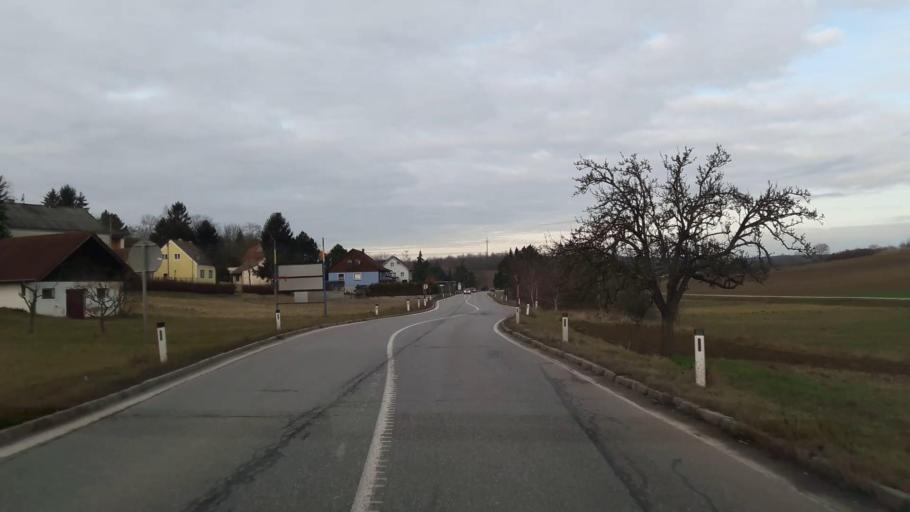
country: AT
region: Lower Austria
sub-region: Politischer Bezirk Mistelbach
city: Asparn an der Zaya
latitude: 48.6122
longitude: 16.5326
